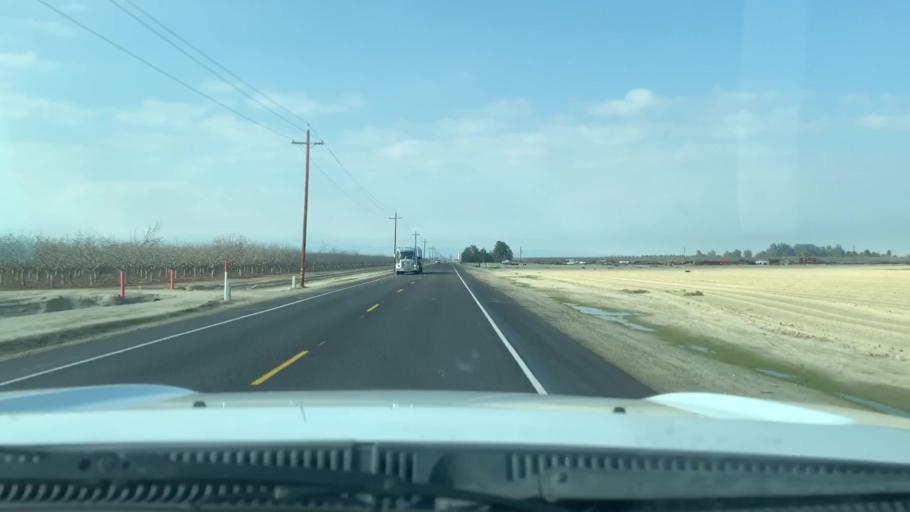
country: US
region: California
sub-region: Kern County
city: Buttonwillow
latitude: 35.4423
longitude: -119.4157
